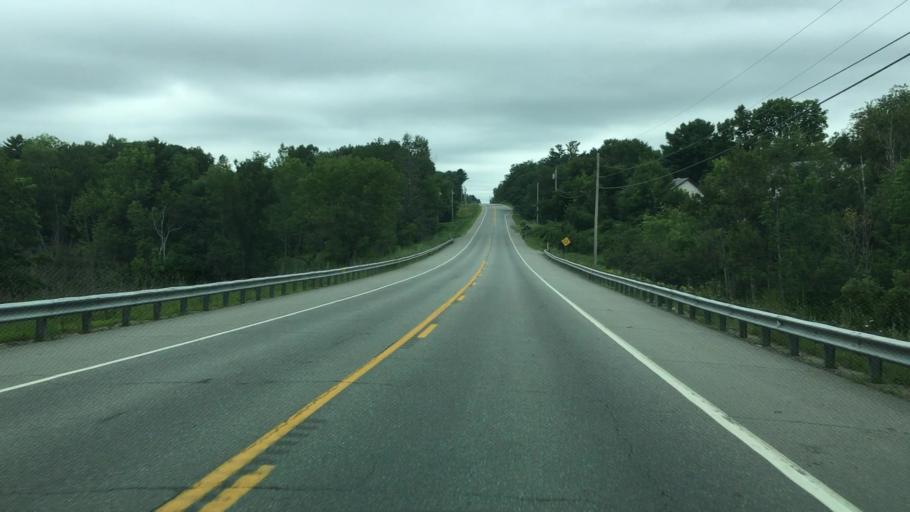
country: US
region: Maine
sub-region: Waldo County
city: Winterport
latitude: 44.6681
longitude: -68.8330
